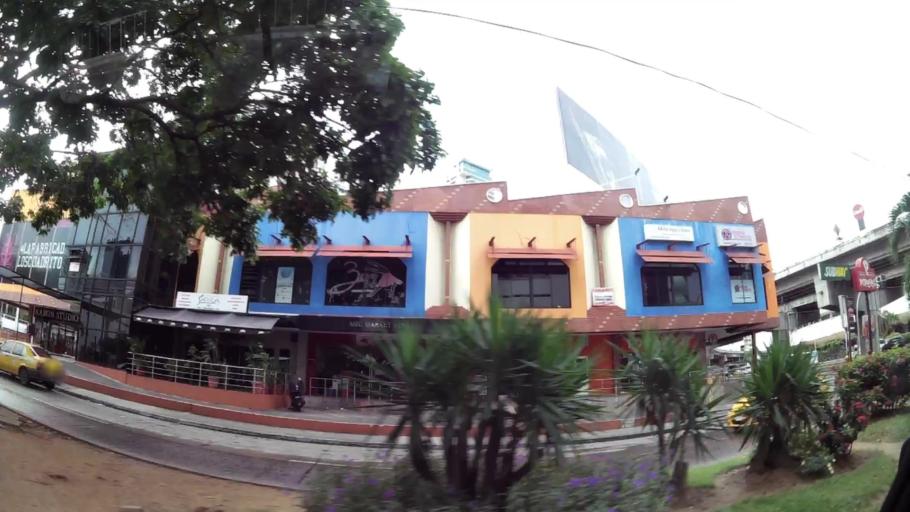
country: PA
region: Panama
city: Panama
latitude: 8.9768
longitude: -79.5157
